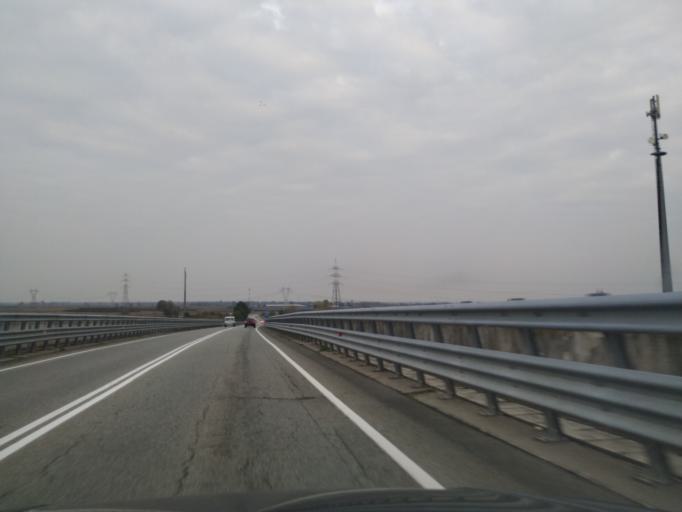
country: IT
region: Piedmont
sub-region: Provincia di Vercelli
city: Borgo d'Ale
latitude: 45.3213
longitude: 8.0734
